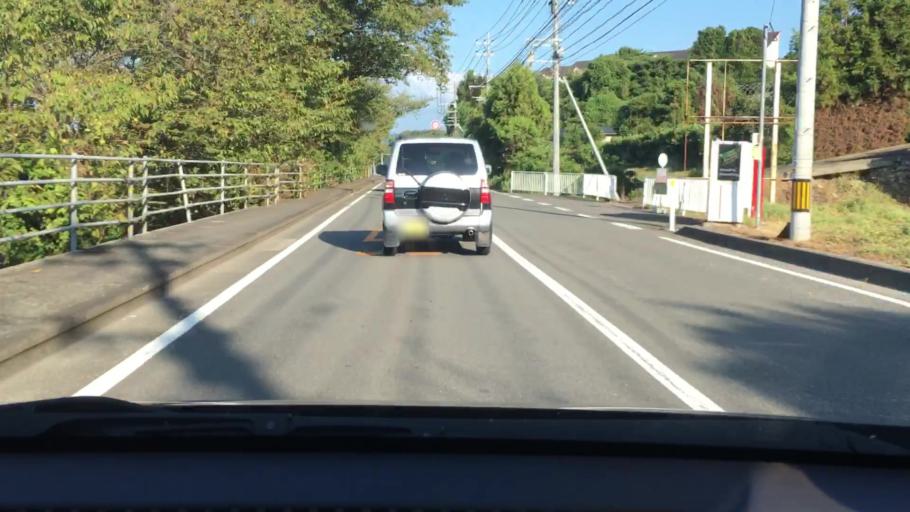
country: JP
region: Nagasaki
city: Togitsu
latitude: 32.8608
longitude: 129.8132
